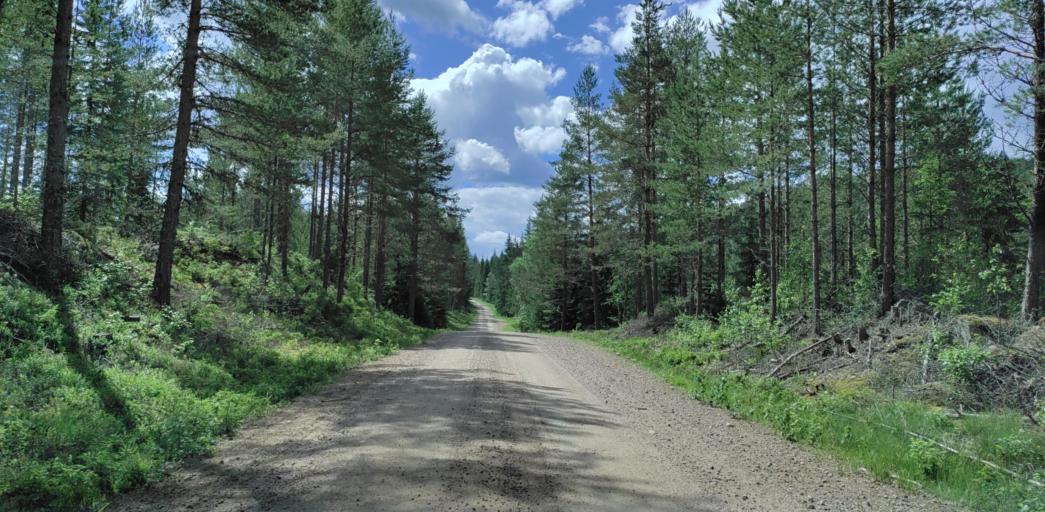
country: SE
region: Vaermland
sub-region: Hagfors Kommun
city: Ekshaerad
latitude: 60.1028
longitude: 13.3547
